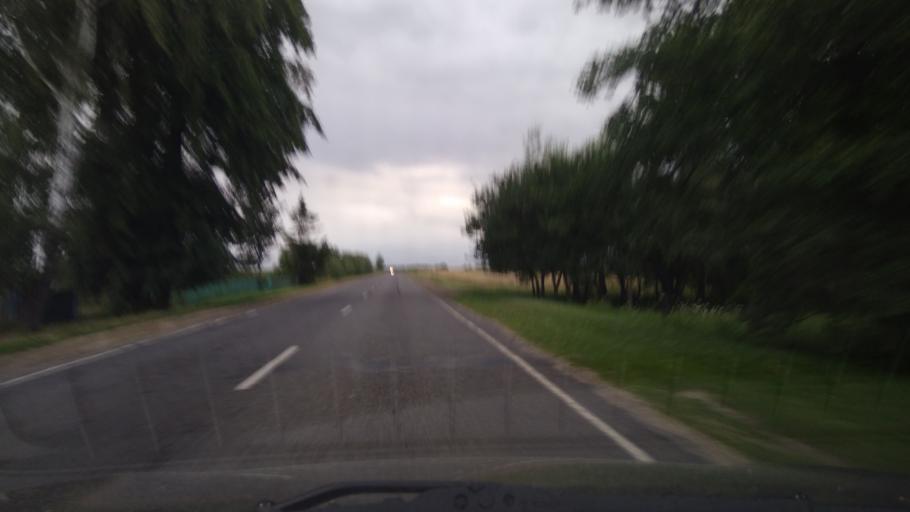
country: BY
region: Brest
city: Byaroza
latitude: 52.4267
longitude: 24.9809
